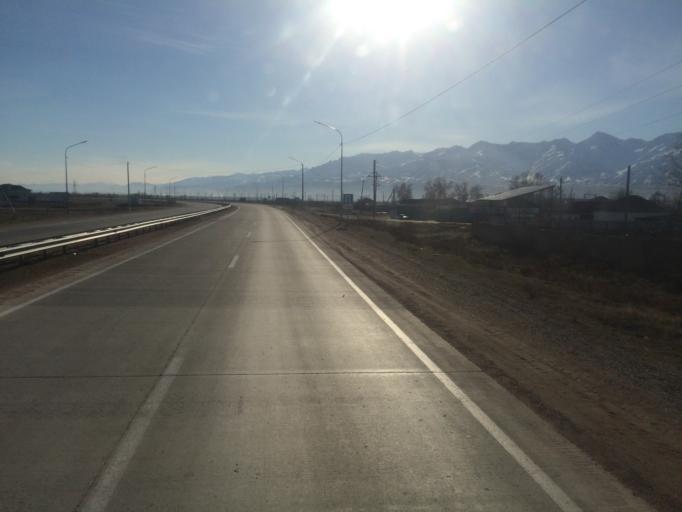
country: KG
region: Talas
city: Ivanovo-Alekseyevka
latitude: 42.9925
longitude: 72.1120
